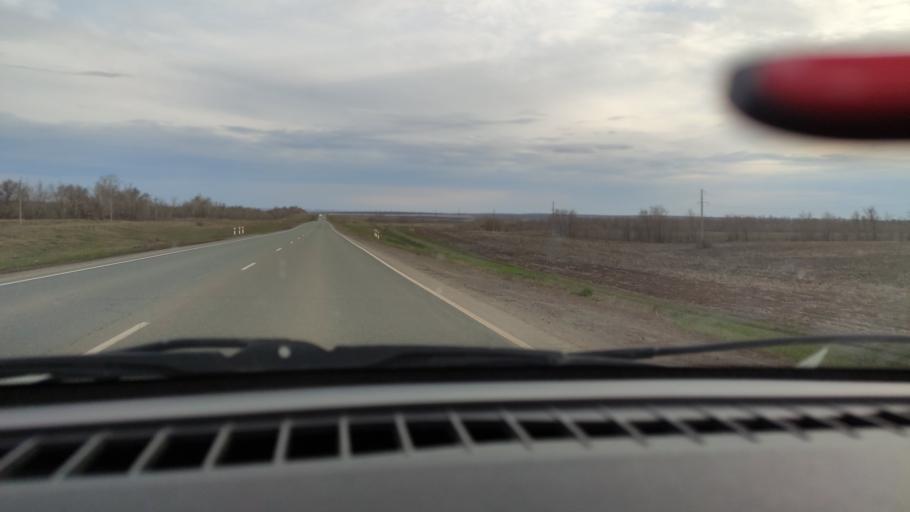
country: RU
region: Orenburg
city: Sakmara
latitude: 52.0535
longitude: 55.2560
